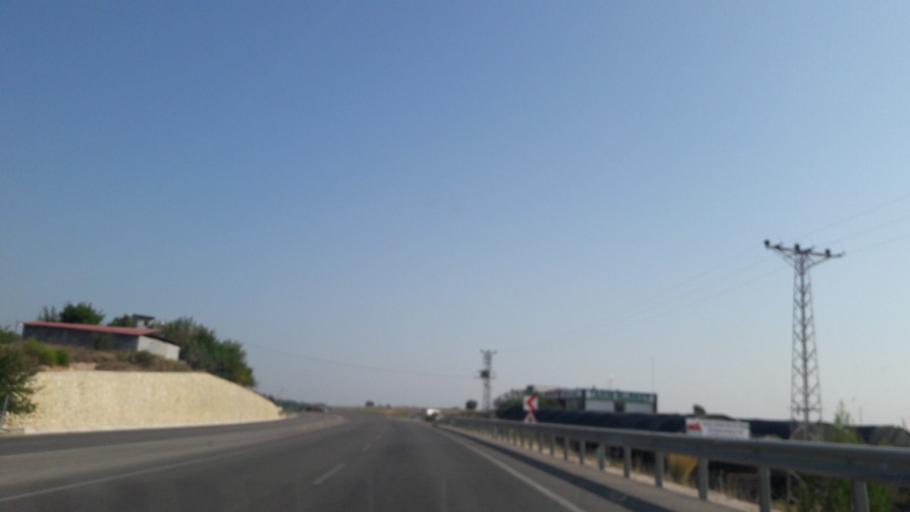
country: TR
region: Adana
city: Sagkaya
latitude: 37.1421
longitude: 35.5392
